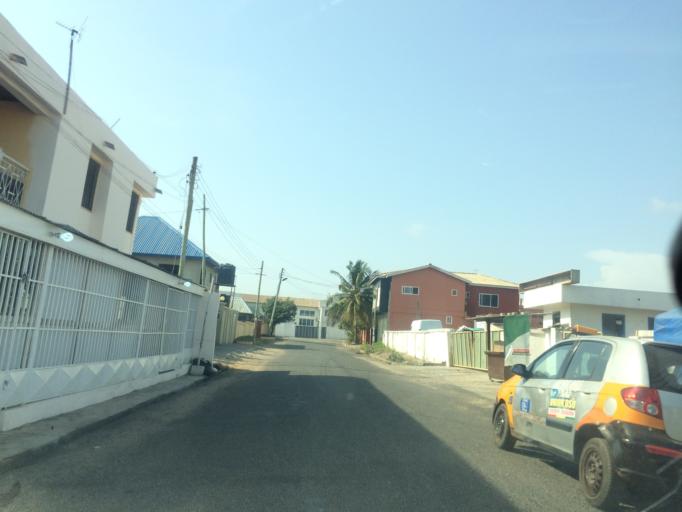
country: GH
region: Greater Accra
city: Accra
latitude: 5.5577
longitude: -0.1716
